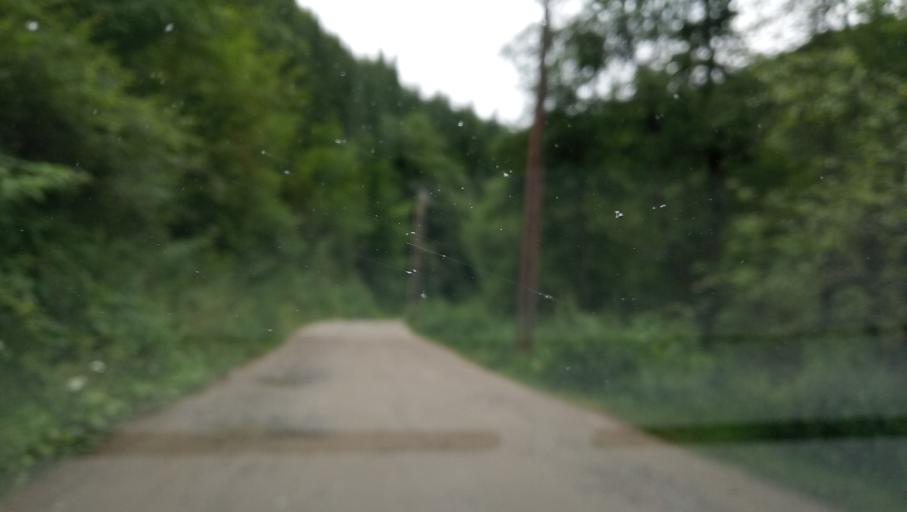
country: RO
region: Hunedoara
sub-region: Oras Petrila
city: Petrila
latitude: 45.4811
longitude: 23.4165
